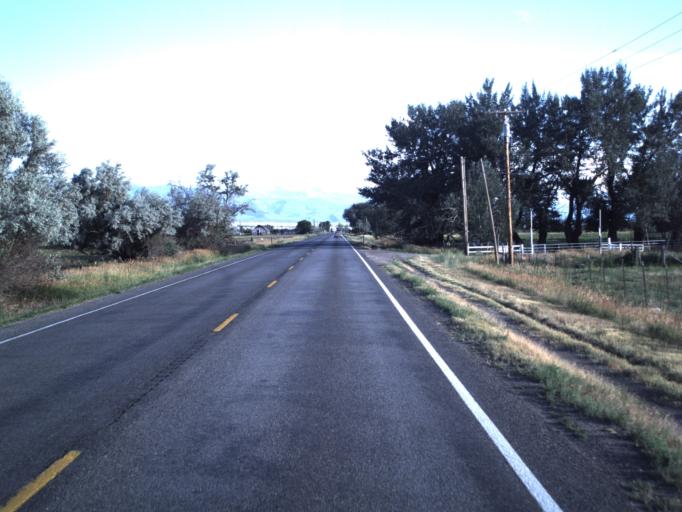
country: US
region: Utah
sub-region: Sanpete County
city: Fairview
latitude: 39.6066
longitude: -111.4448
